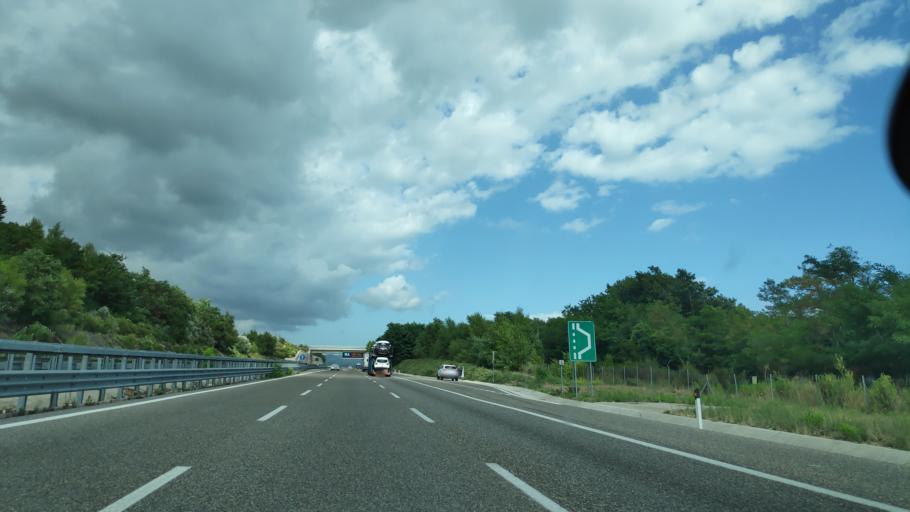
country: IT
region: Campania
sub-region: Provincia di Salerno
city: Contursi Terme
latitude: 40.6147
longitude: 15.2645
